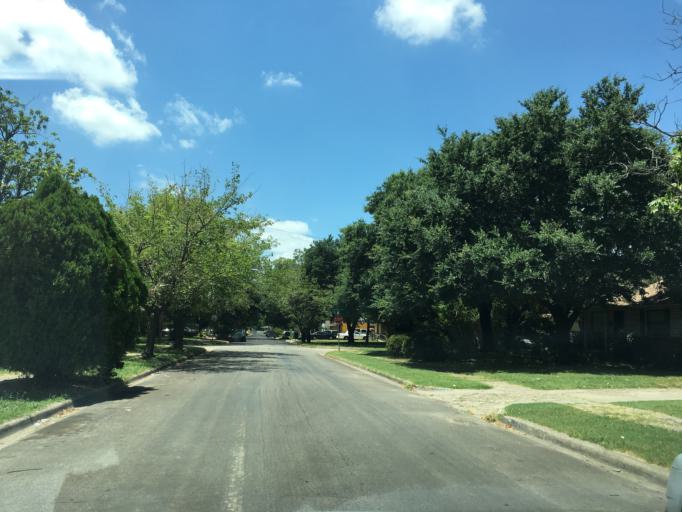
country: US
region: Texas
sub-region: Dallas County
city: Garland
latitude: 32.8386
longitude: -96.6677
